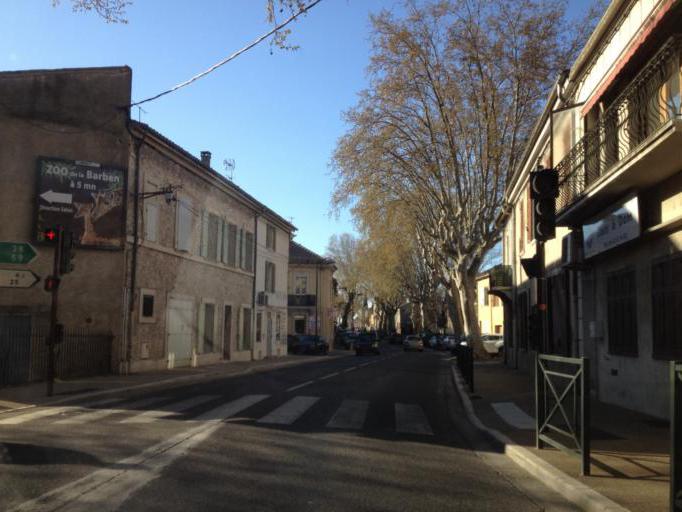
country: FR
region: Provence-Alpes-Cote d'Azur
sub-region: Departement des Bouches-du-Rhone
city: Saint-Cannat
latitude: 43.6213
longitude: 5.2978
